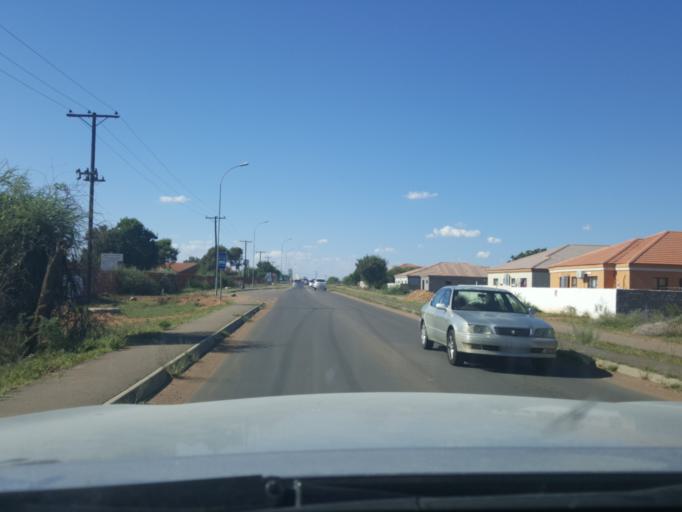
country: BW
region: South East
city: Gaborone
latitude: -24.6131
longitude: 25.9502
